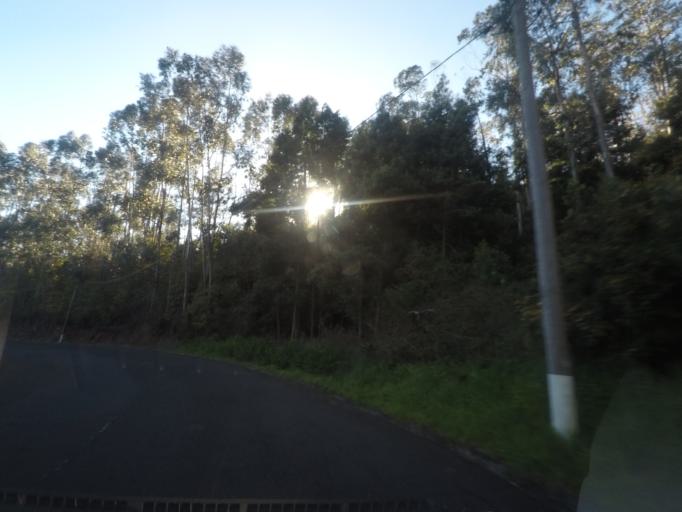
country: PT
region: Madeira
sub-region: Santa Cruz
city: Camacha
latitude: 32.6718
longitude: -16.8643
